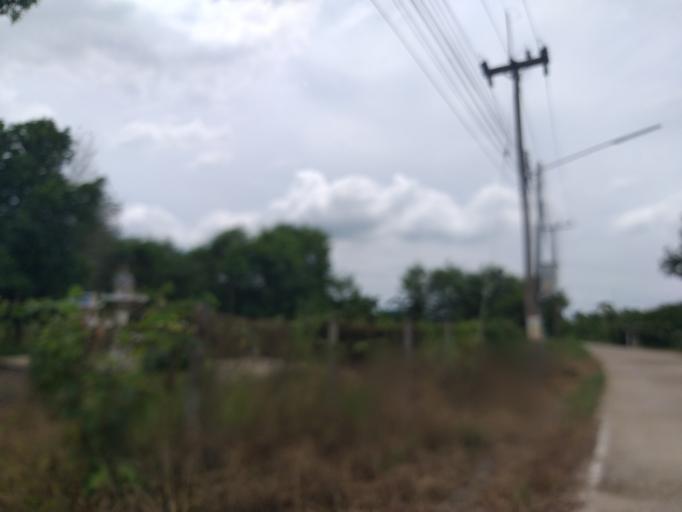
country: TH
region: Pathum Thani
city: Ban Lam Luk Ka
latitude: 13.9822
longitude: 100.8543
